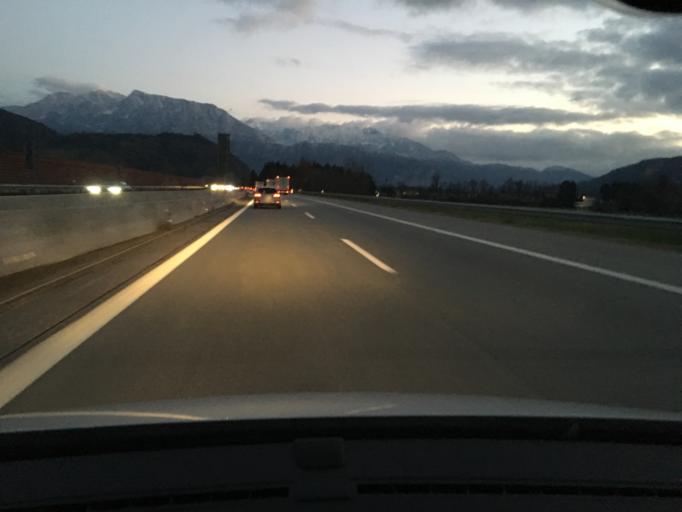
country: AT
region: Tyrol
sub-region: Politischer Bezirk Kufstein
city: Erl
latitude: 47.6776
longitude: 12.1692
